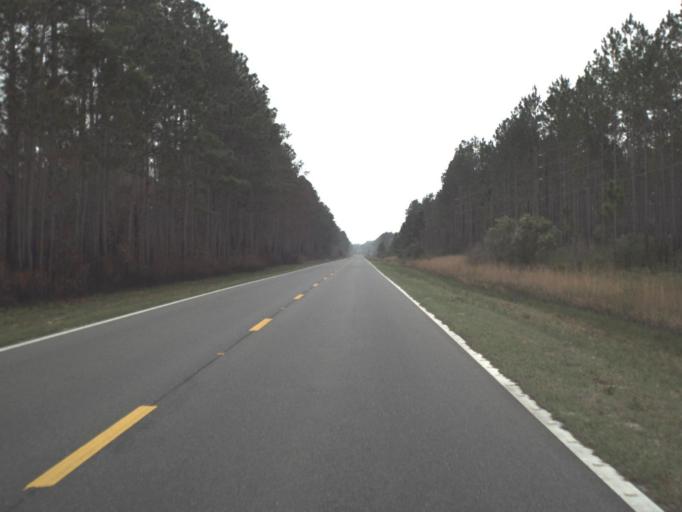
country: US
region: Florida
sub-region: Liberty County
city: Bristol
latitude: 30.2896
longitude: -84.8367
